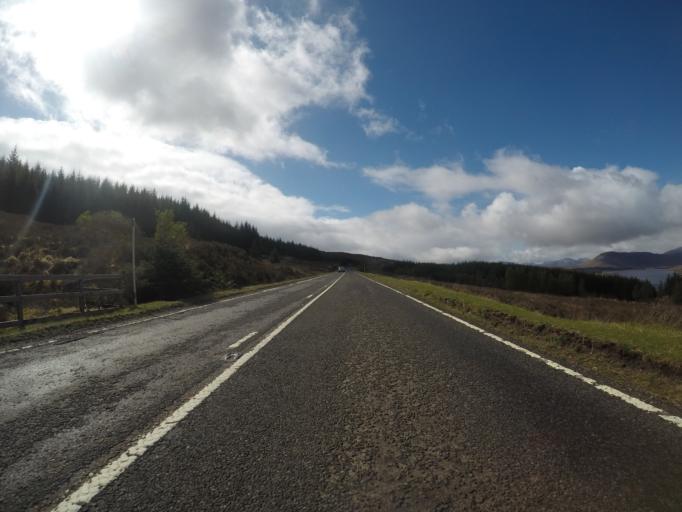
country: GB
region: Scotland
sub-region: Highland
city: Spean Bridge
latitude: 57.1108
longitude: -4.9838
